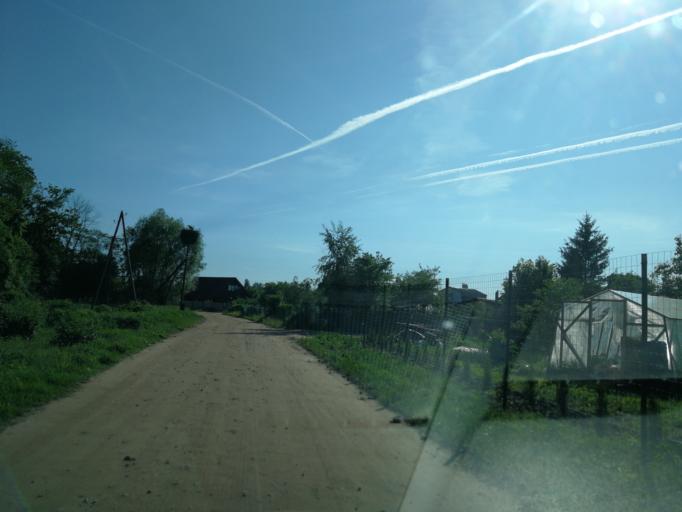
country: LV
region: Adazi
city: Adazi
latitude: 57.0932
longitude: 24.3228
